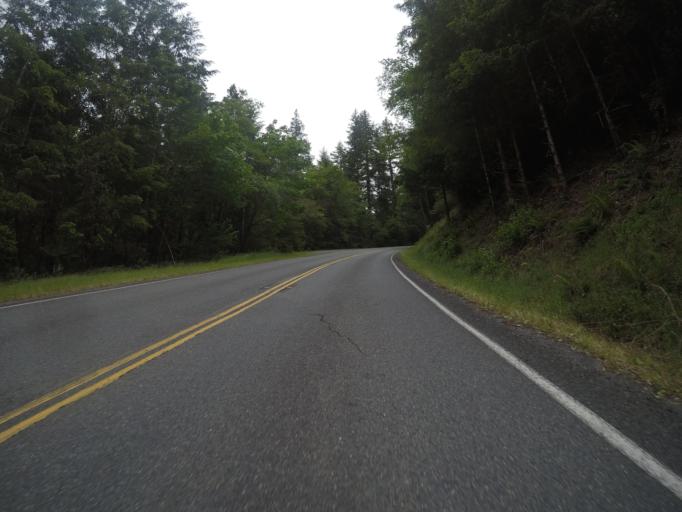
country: US
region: California
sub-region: Del Norte County
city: Bertsch-Oceanview
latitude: 41.7795
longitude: -124.0145
